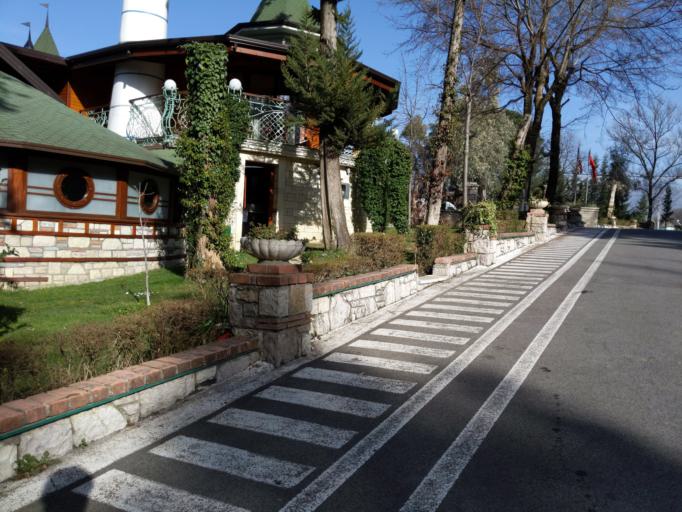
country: AL
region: Tirane
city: Tirana
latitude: 41.3134
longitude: 19.8331
